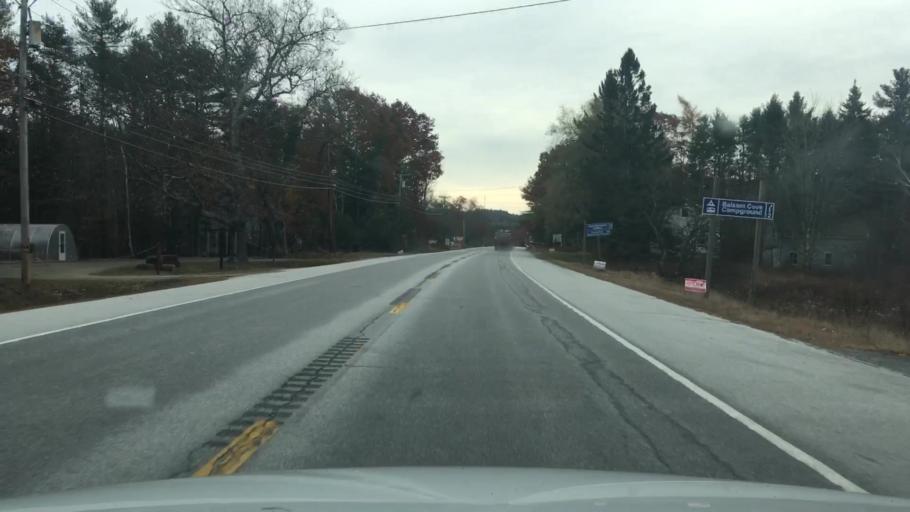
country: US
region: Maine
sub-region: Hancock County
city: Orland
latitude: 44.5658
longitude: -68.7174
